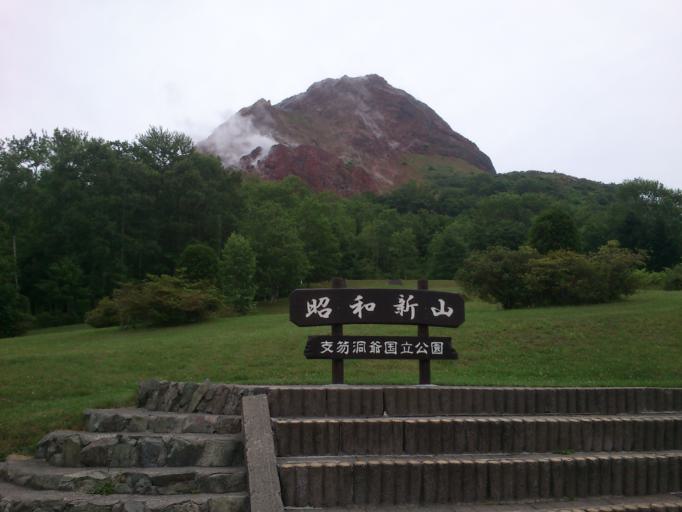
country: JP
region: Hokkaido
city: Date
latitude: 42.5406
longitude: 140.8594
